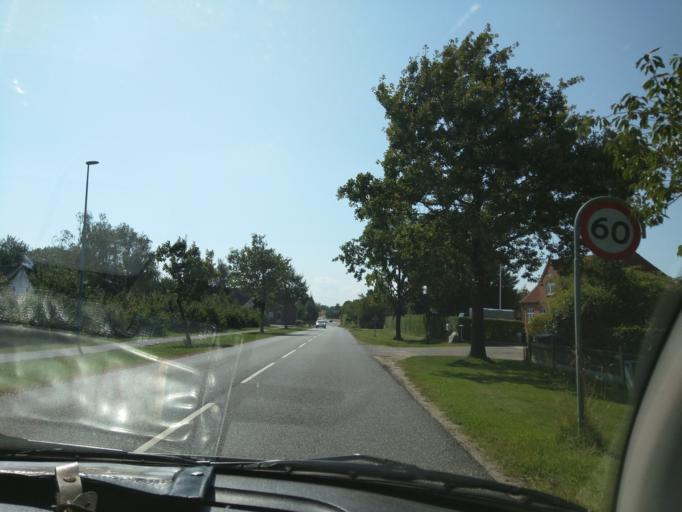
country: DK
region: Central Jutland
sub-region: Viborg Kommune
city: Bjerringbro
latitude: 56.2652
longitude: 9.7195
